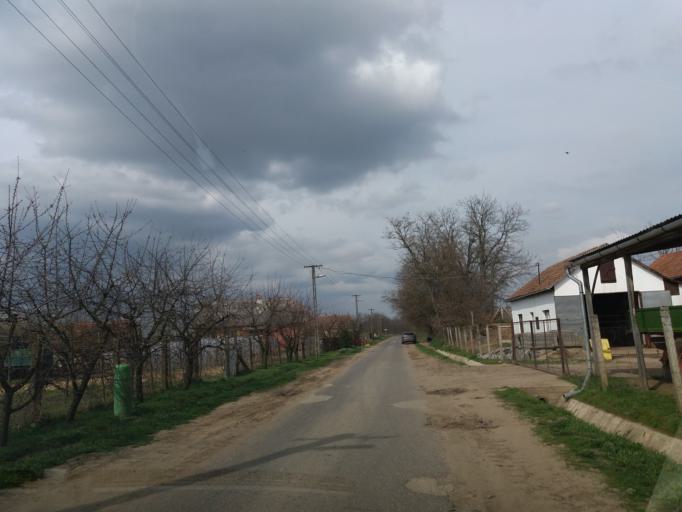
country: HU
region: Szabolcs-Szatmar-Bereg
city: Petnehaza
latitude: 48.0617
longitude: 22.0456
